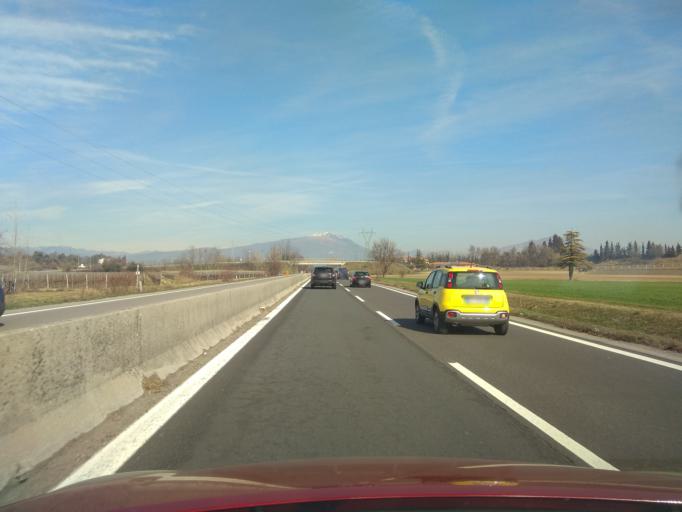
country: IT
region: Veneto
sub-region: Provincia di Verona
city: Cola
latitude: 45.4816
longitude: 10.7649
